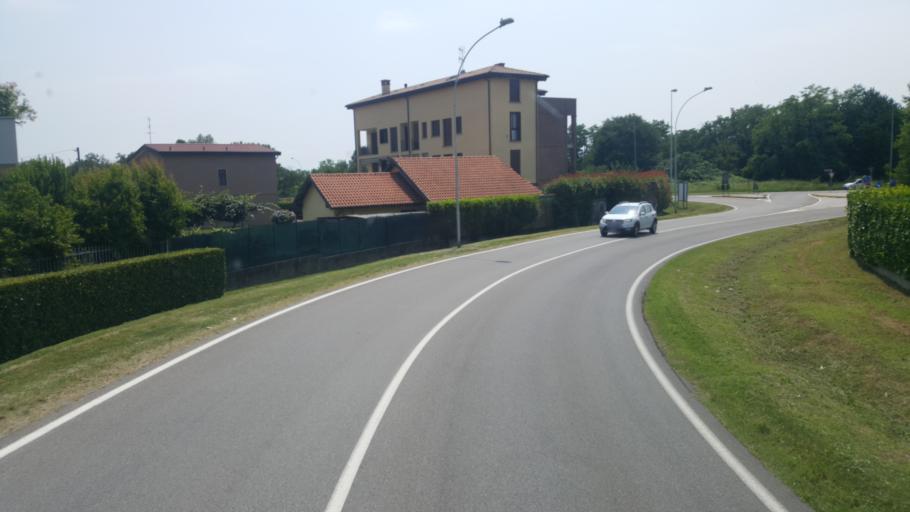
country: IT
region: Lombardy
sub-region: Provincia di Monza e Brianza
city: Burago di Molgora
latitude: 45.5961
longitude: 9.3764
